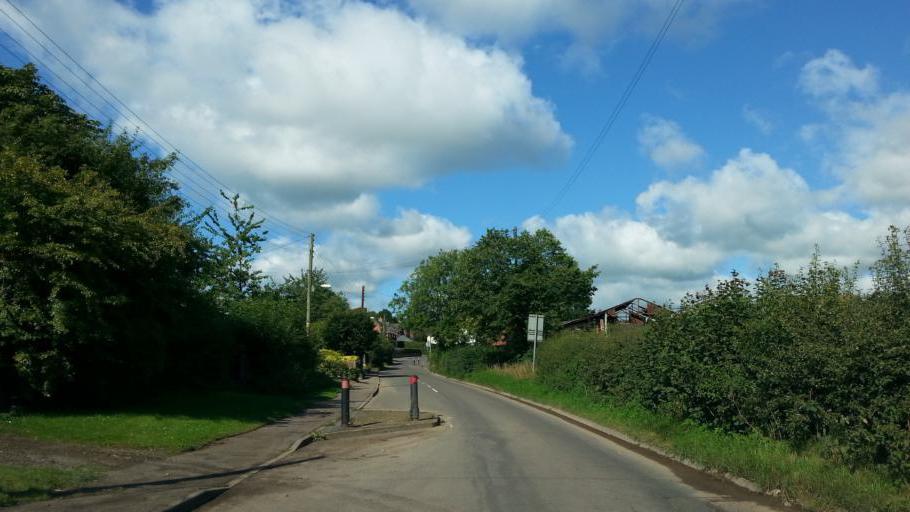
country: GB
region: England
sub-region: Staffordshire
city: Armitage
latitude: 52.8162
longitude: -1.8701
